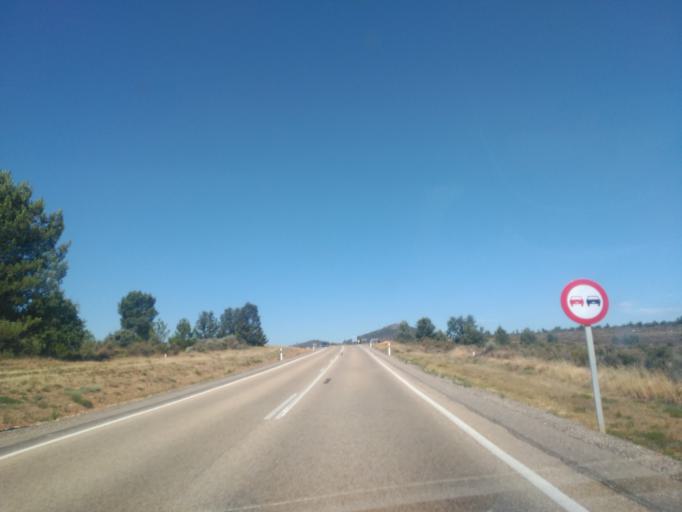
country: ES
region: Castille and Leon
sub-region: Provincia de Zamora
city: Otero de Bodas
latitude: 41.9342
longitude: -6.1248
